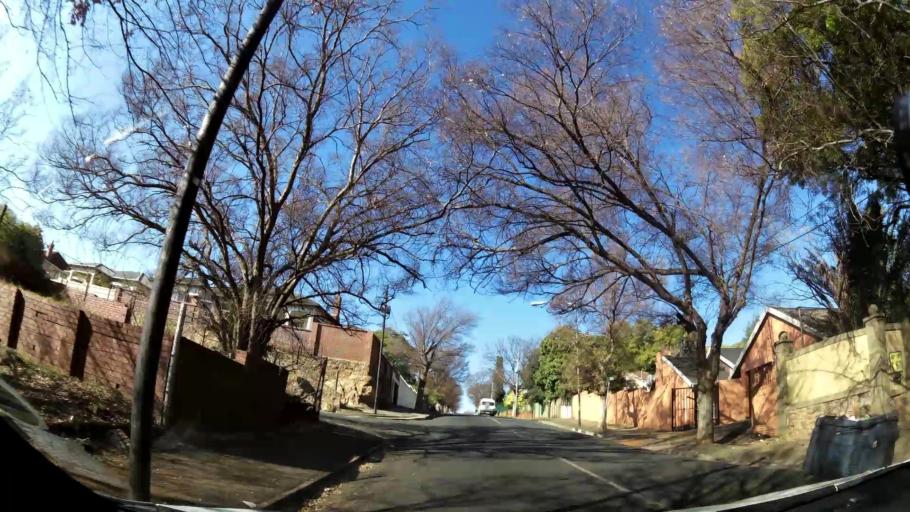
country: ZA
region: Gauteng
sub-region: City of Johannesburg Metropolitan Municipality
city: Johannesburg
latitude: -26.1984
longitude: 28.0977
